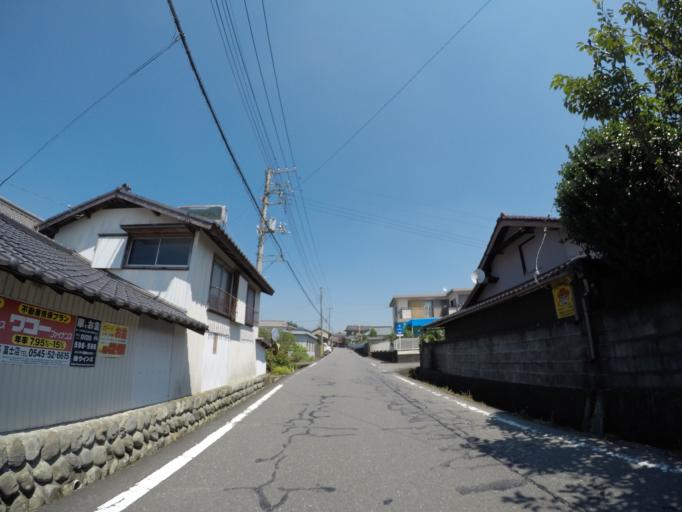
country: JP
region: Shizuoka
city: Fujinomiya
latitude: 35.2261
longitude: 138.5659
